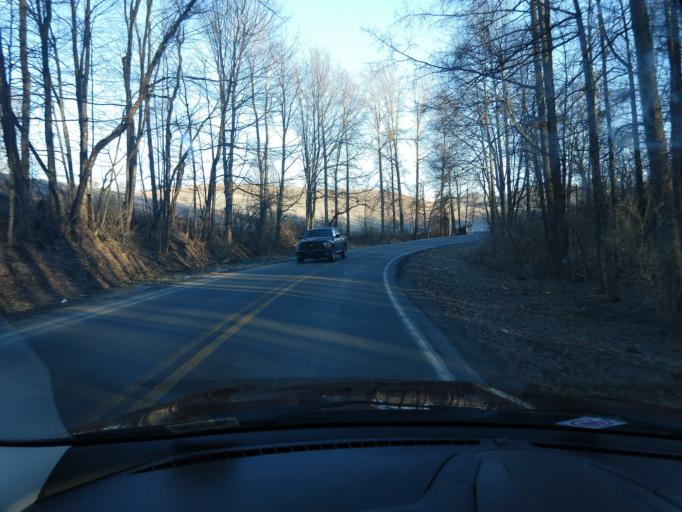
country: US
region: West Virginia
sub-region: Greenbrier County
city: Rainelle
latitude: 37.8611
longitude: -80.7191
